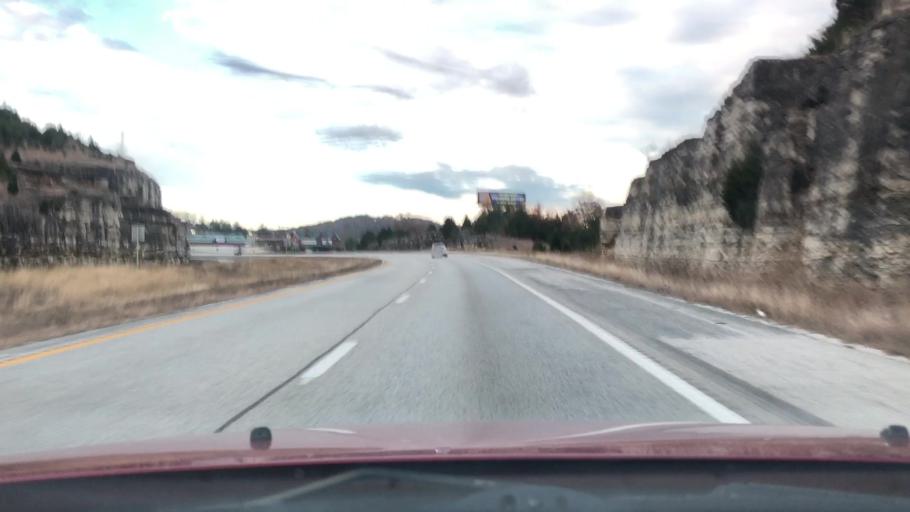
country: US
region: Missouri
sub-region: Taney County
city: Merriam Woods
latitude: 36.8243
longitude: -93.2249
